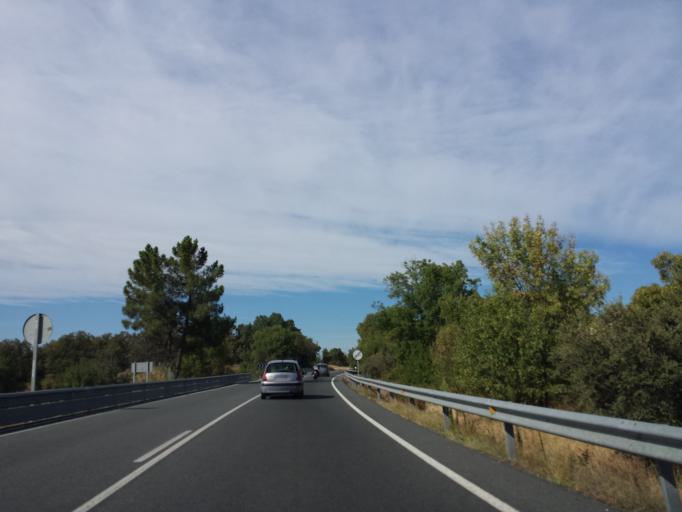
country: ES
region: Castille and Leon
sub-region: Provincia de Avila
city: Casavieja
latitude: 40.2755
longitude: -4.7411
